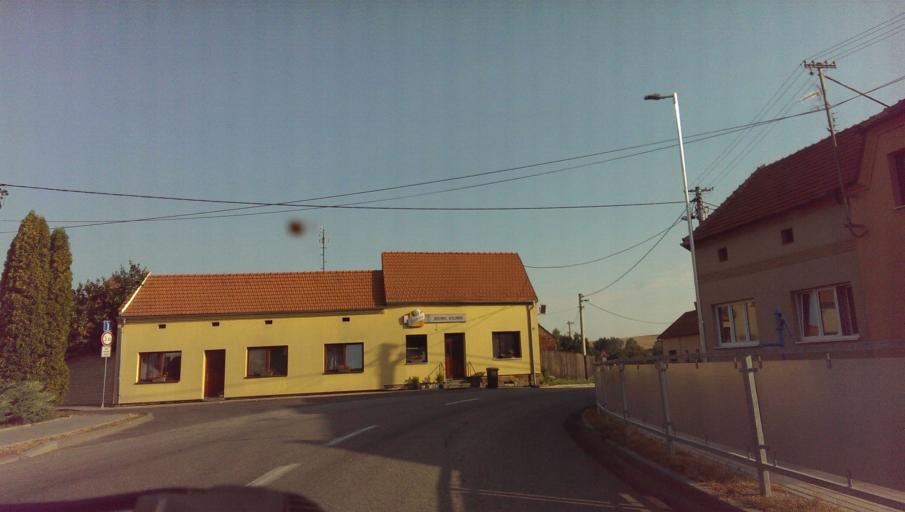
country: CZ
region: Zlin
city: Korycany
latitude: 49.1127
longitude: 17.1348
